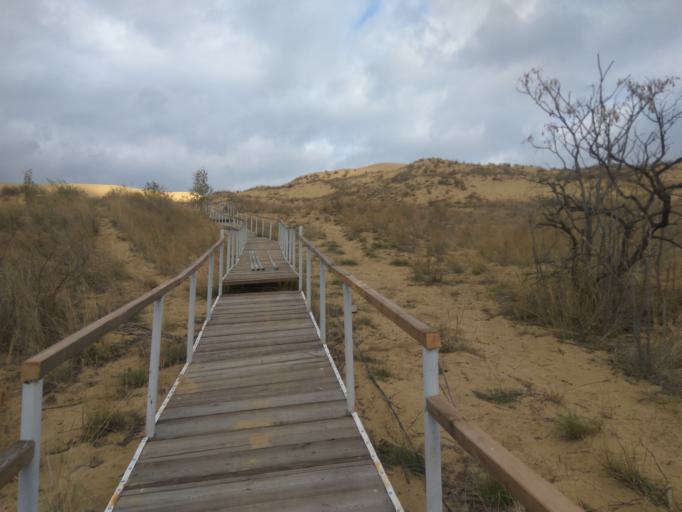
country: RU
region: Dagestan
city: Korkmaskala
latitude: 43.0047
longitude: 47.2365
